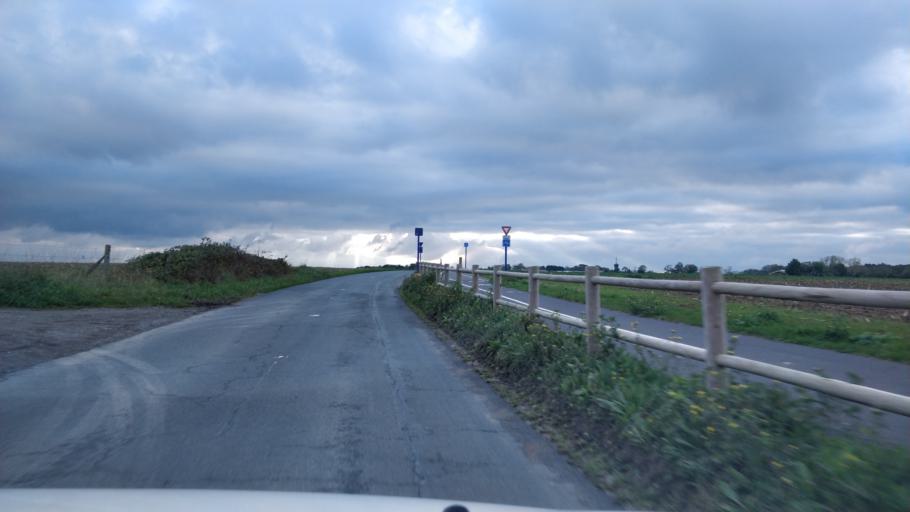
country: FR
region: Lower Normandy
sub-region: Departement du Calvados
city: Ouistreham
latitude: 49.2667
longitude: -0.2704
